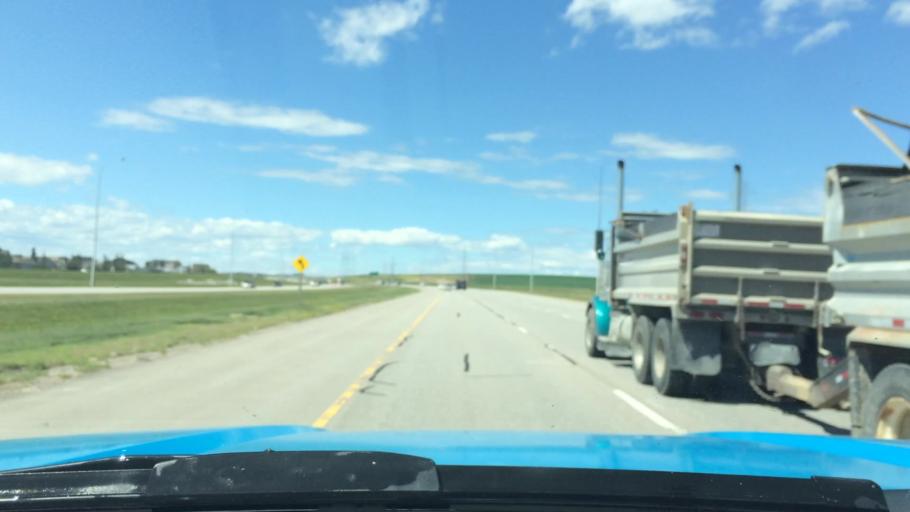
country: CA
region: Alberta
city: Airdrie
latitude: 51.1757
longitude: -114.0383
